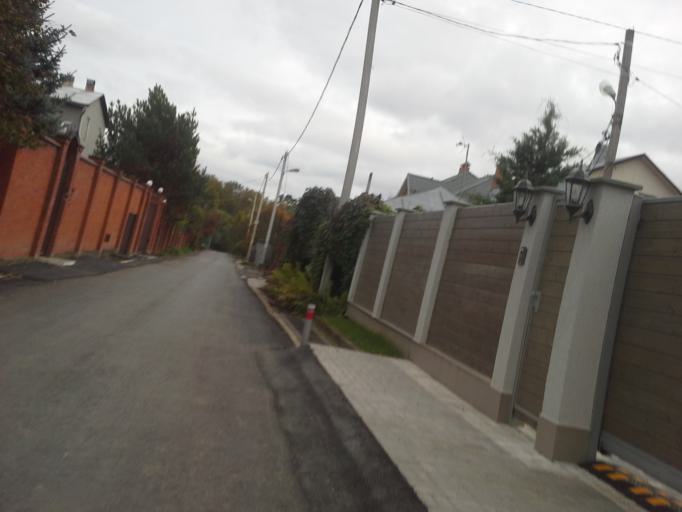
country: RU
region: Moskovskaya
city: Kokoshkino
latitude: 55.6183
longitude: 37.1631
